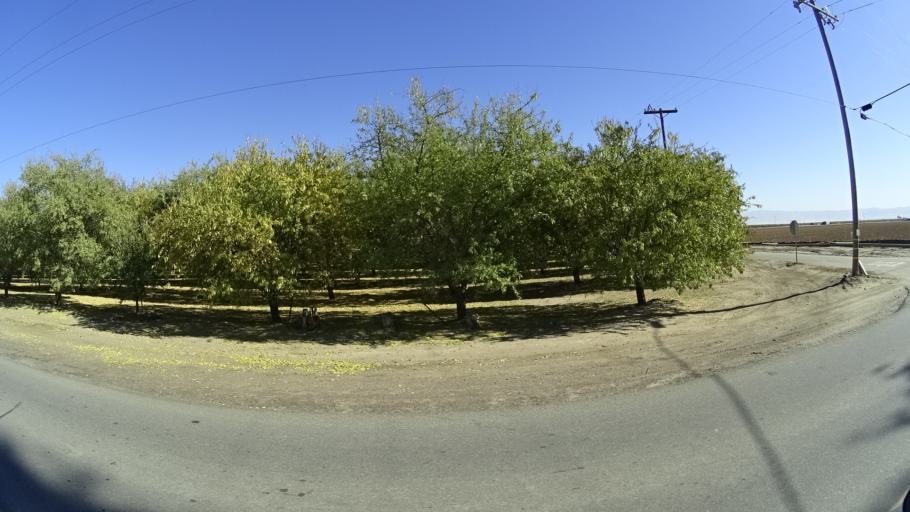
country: US
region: California
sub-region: Kern County
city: Greenfield
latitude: 35.2529
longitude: -119.0745
